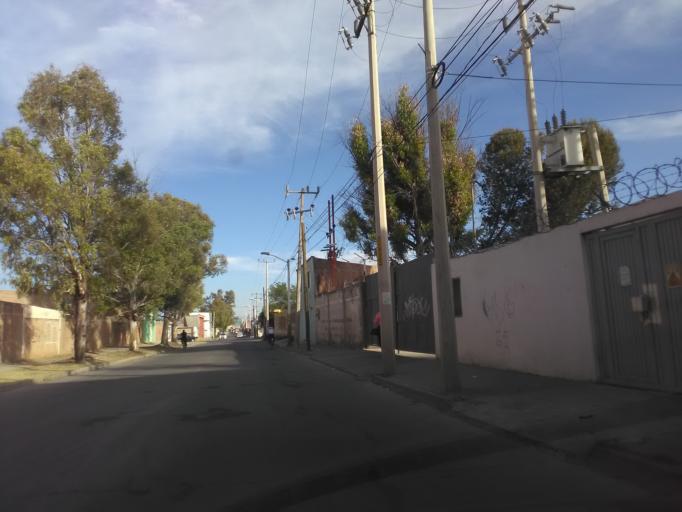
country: MX
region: Durango
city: Victoria de Durango
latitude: 24.0246
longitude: -104.6285
